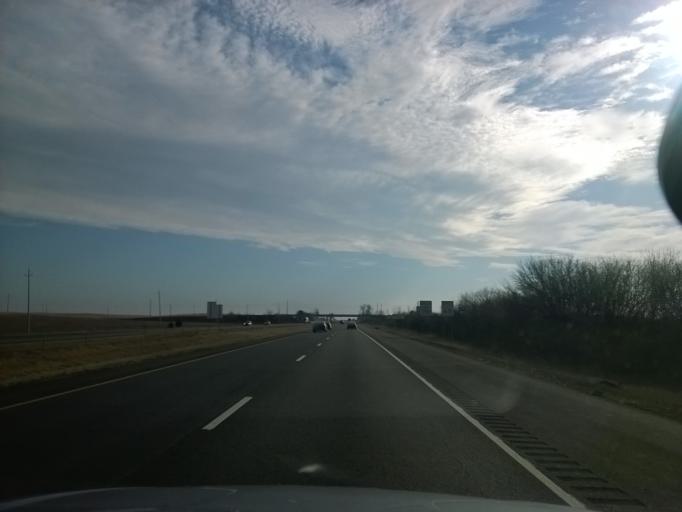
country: US
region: Indiana
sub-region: Johnson County
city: Edinburgh
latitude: 39.3522
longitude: -85.9425
